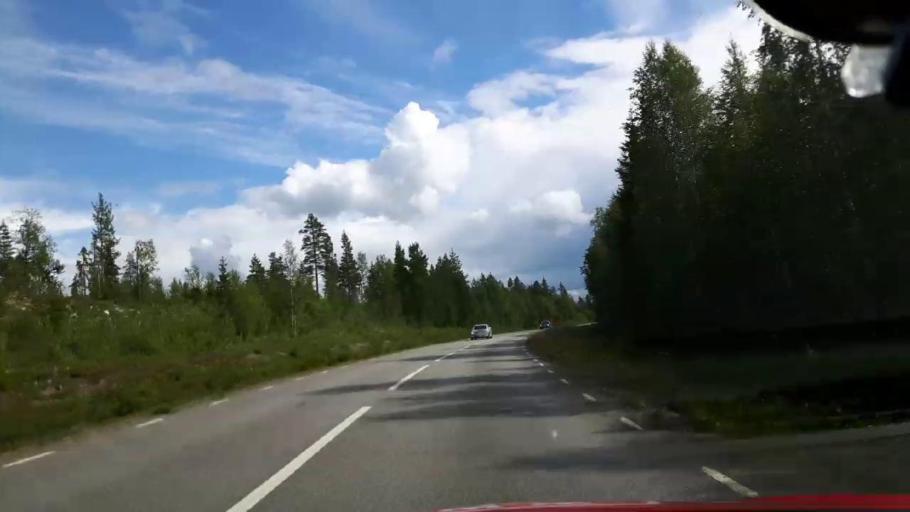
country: SE
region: Jaemtland
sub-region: Stroemsunds Kommun
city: Stroemsund
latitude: 64.3451
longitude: 15.1038
